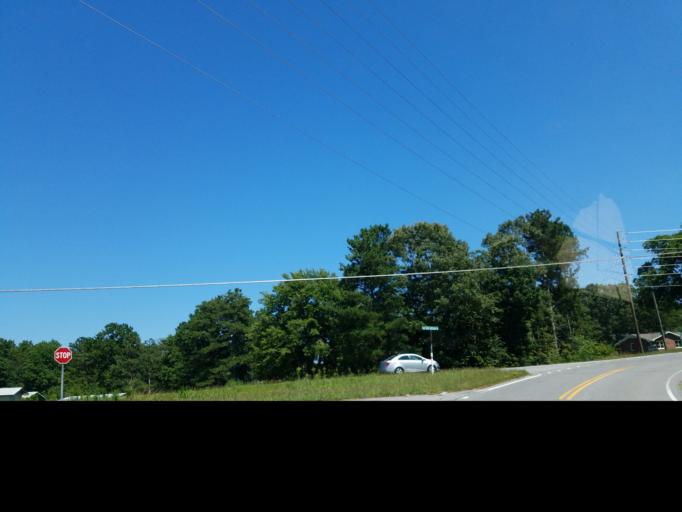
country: US
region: Georgia
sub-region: Dawson County
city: Dawsonville
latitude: 34.3281
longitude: -84.0493
